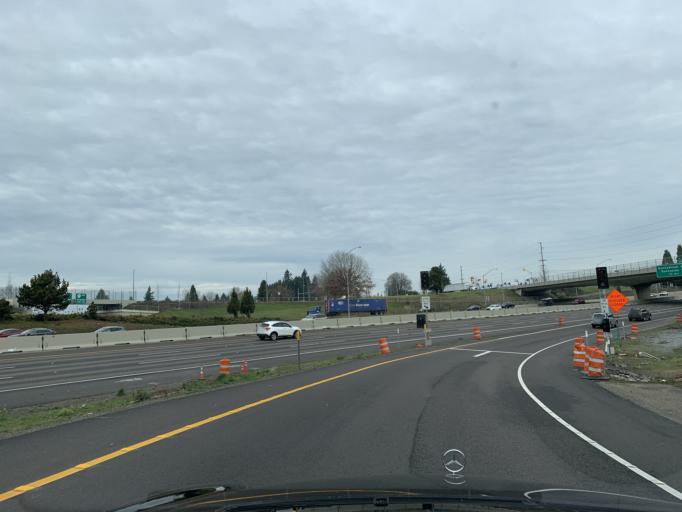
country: US
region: Oregon
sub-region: Clackamas County
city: Clackamas
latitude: 45.4189
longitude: -122.5731
